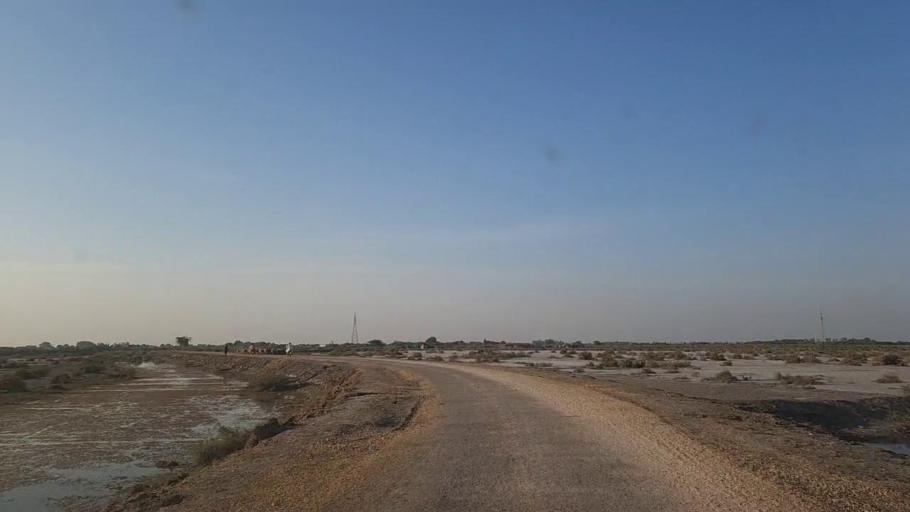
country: PK
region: Sindh
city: Mirpur Batoro
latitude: 24.6899
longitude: 68.2027
